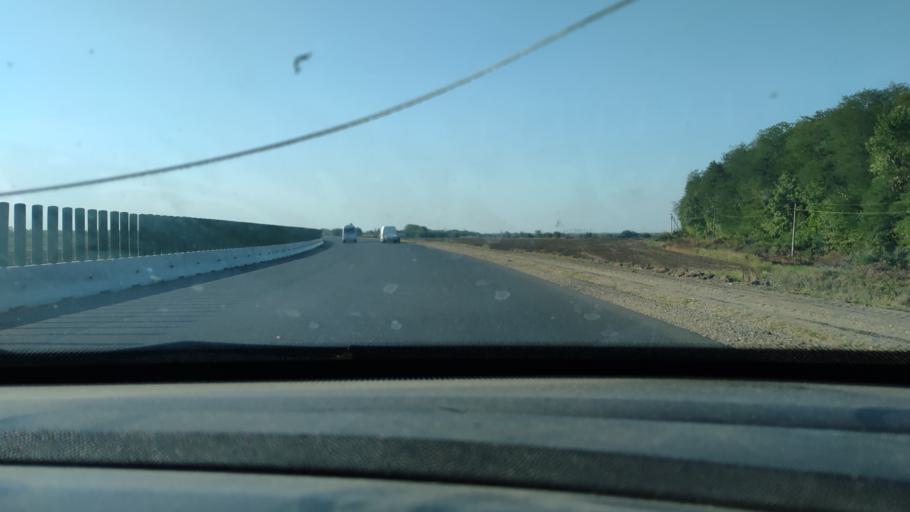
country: RU
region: Krasnodarskiy
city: Medvedovskaya
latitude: 45.4689
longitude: 38.9803
